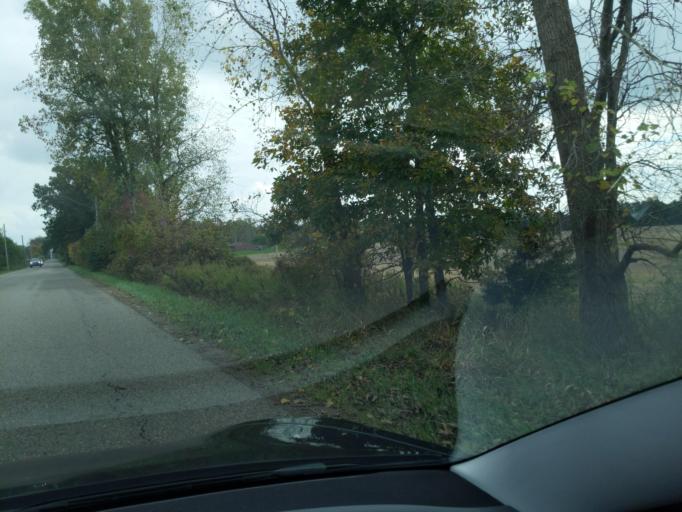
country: US
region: Michigan
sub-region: Eaton County
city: Eaton Rapids
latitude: 42.4919
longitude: -84.6528
